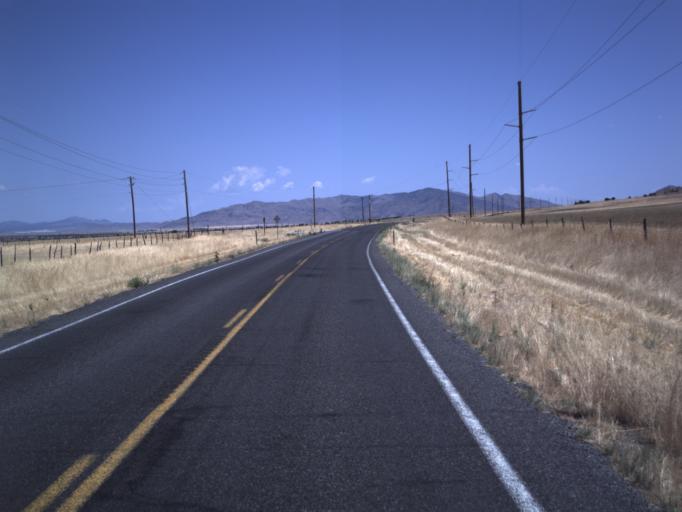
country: US
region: Utah
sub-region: Millard County
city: Delta
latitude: 39.4264
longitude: -112.3262
